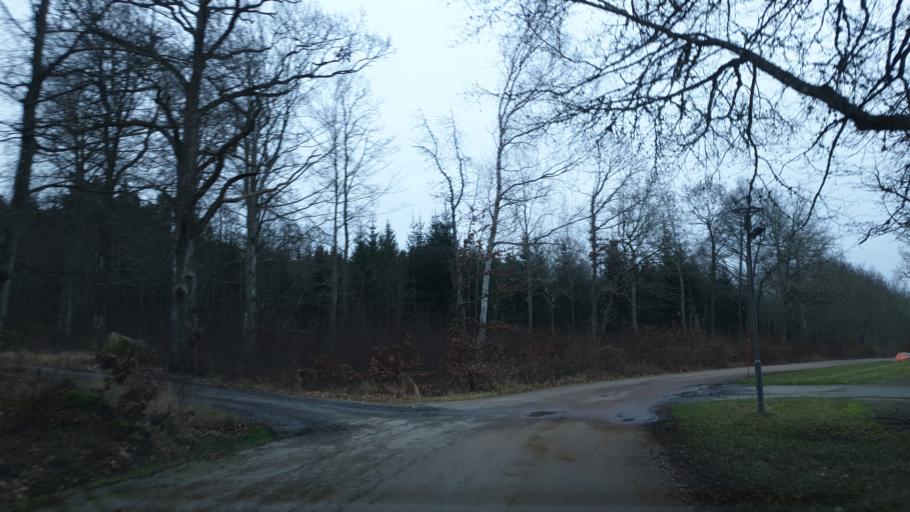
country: SE
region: Blekinge
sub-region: Karlskrona Kommun
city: Rodeby
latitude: 56.2144
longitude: 15.6840
